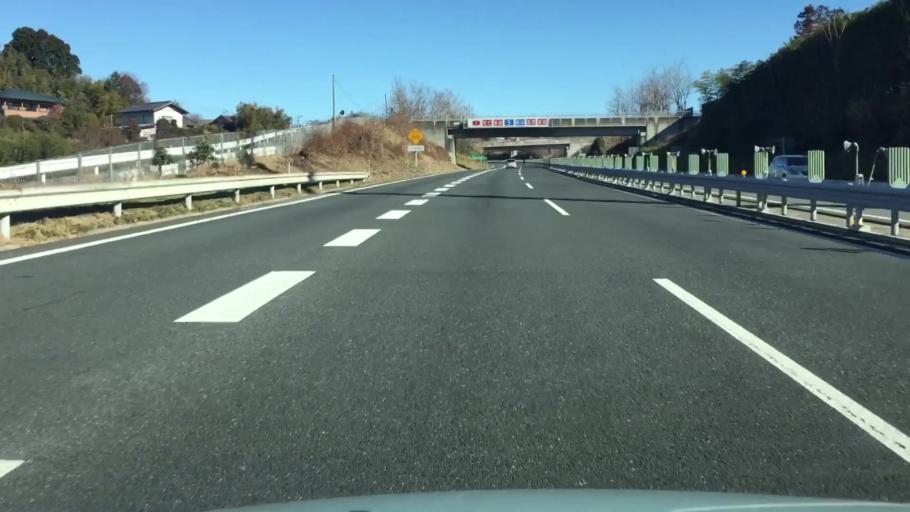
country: JP
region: Gunma
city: Shibukawa
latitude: 36.5154
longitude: 139.0342
